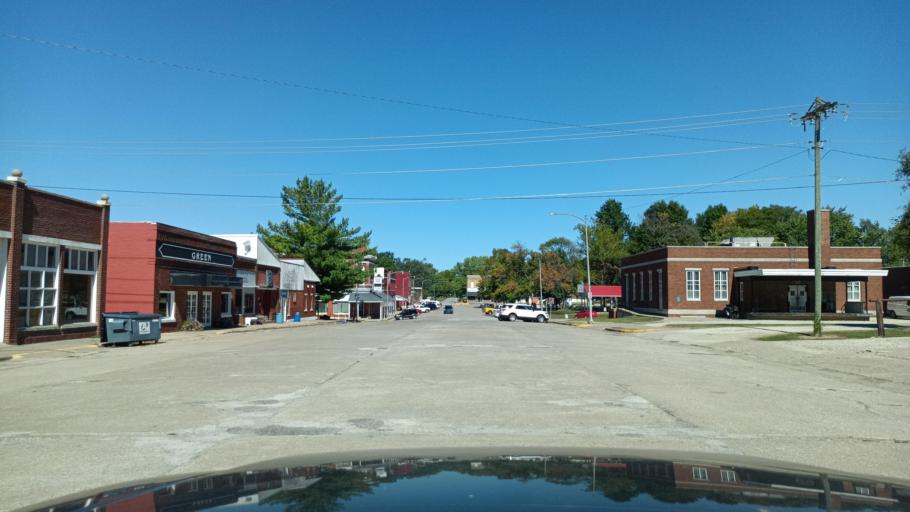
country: US
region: Missouri
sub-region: Macon County
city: La Plata
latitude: 40.0213
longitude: -92.4916
